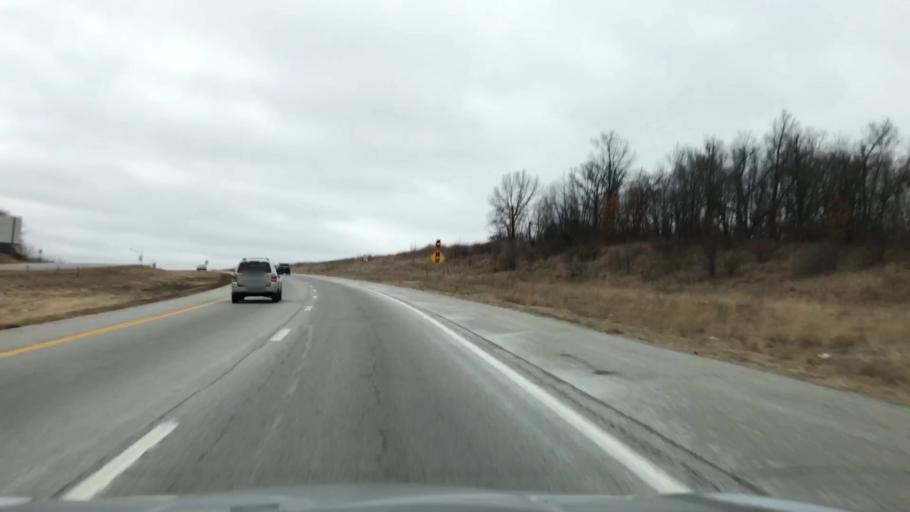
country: US
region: Missouri
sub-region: Jackson County
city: East Independence
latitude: 39.0578
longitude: -94.3677
